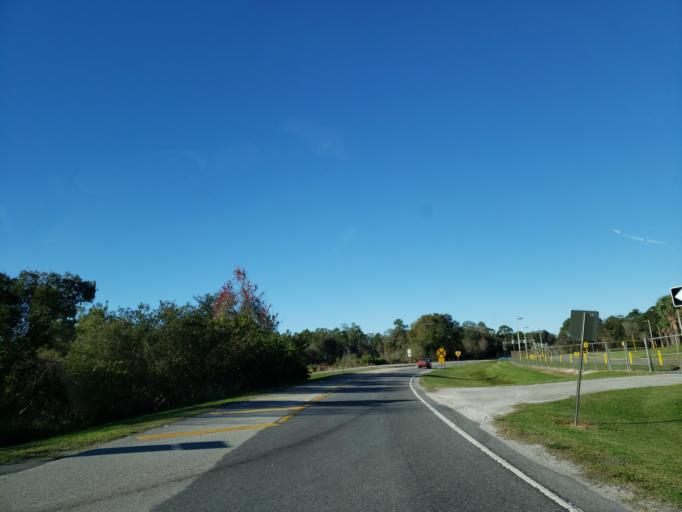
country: US
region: Florida
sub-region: Hillsborough County
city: Plant City
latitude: 27.9968
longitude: -82.1069
